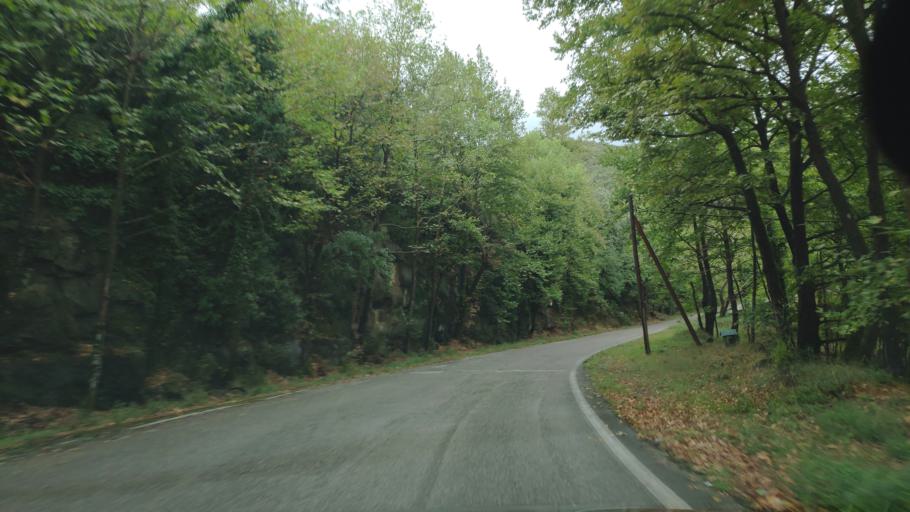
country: GR
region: West Greece
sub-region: Nomos Aitolias kai Akarnanias
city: Sardinia
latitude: 38.9439
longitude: 21.3393
